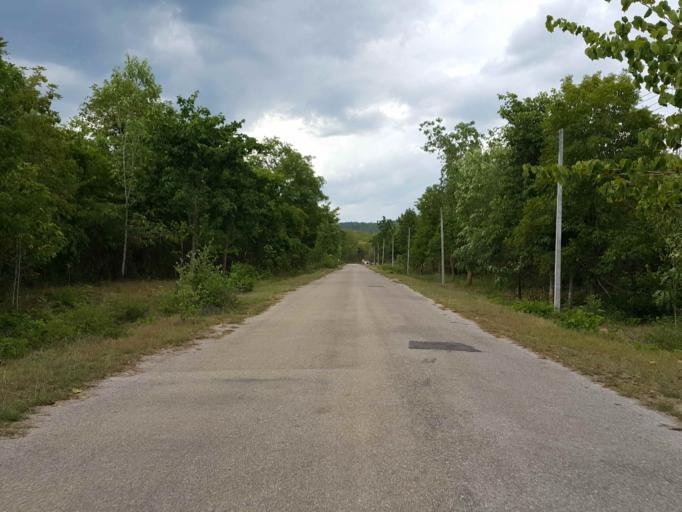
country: TH
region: Sukhothai
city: Thung Saliam
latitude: 17.3462
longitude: 99.4237
